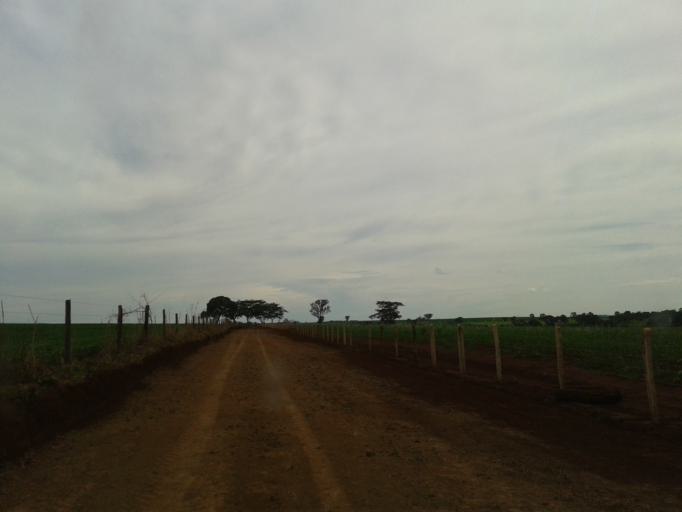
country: BR
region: Minas Gerais
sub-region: Centralina
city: Centralina
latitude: -18.6685
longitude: -49.3477
